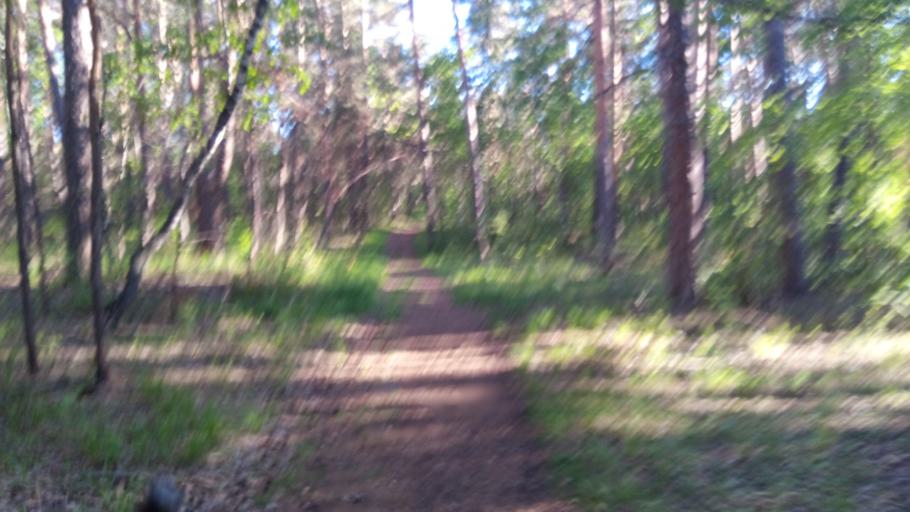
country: RU
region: Chelyabinsk
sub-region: Gorod Chelyabinsk
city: Chelyabinsk
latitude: 55.1312
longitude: 61.3351
